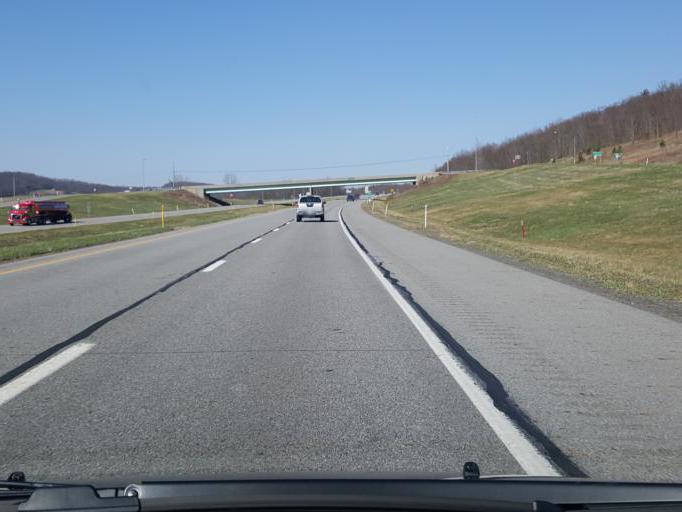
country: US
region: Pennsylvania
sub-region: Blair County
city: Claysburg
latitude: 40.1906
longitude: -78.4882
